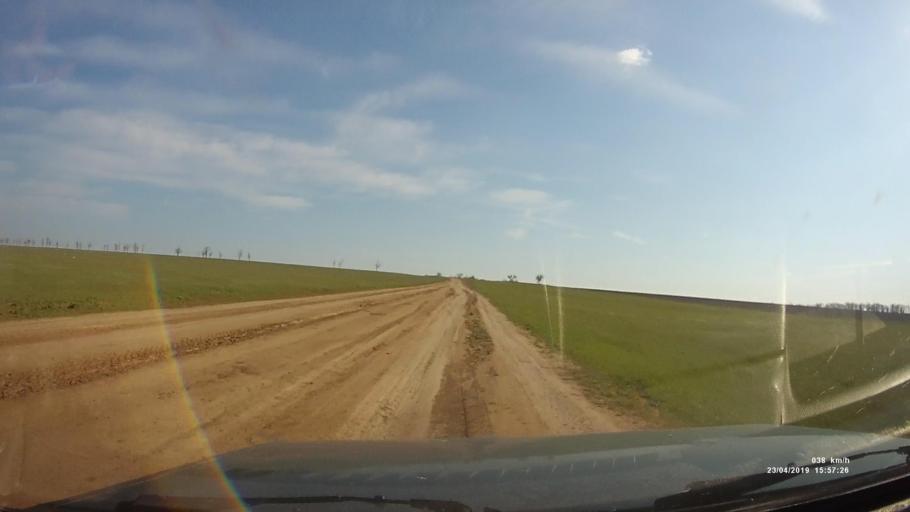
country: RU
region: Rostov
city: Remontnoye
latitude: 46.5318
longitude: 43.1099
